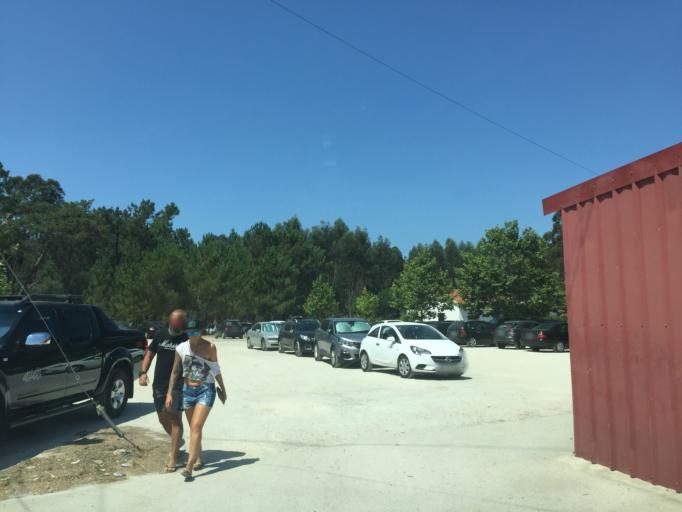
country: PT
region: Coimbra
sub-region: Mira
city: Mira
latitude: 40.3415
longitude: -8.7275
